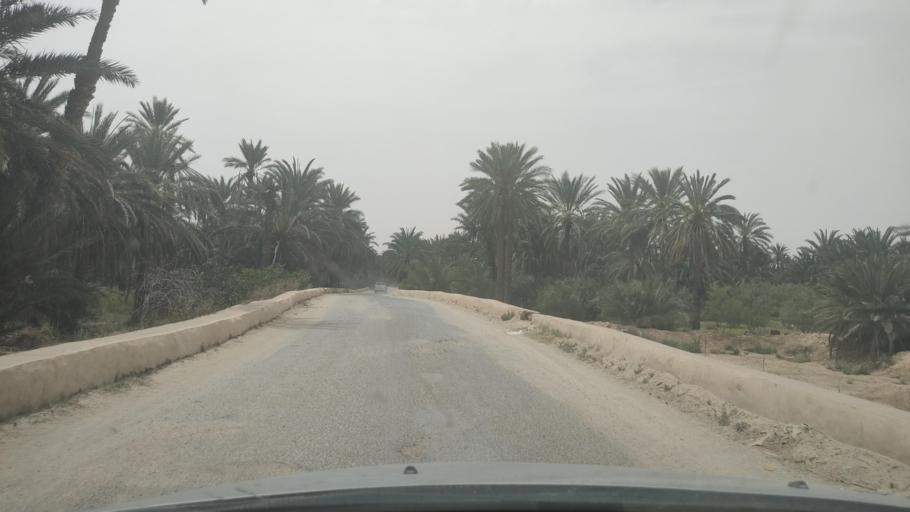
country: TN
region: Gafsa
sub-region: Gafsa Municipality
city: Gafsa
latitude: 34.3287
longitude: 8.9523
